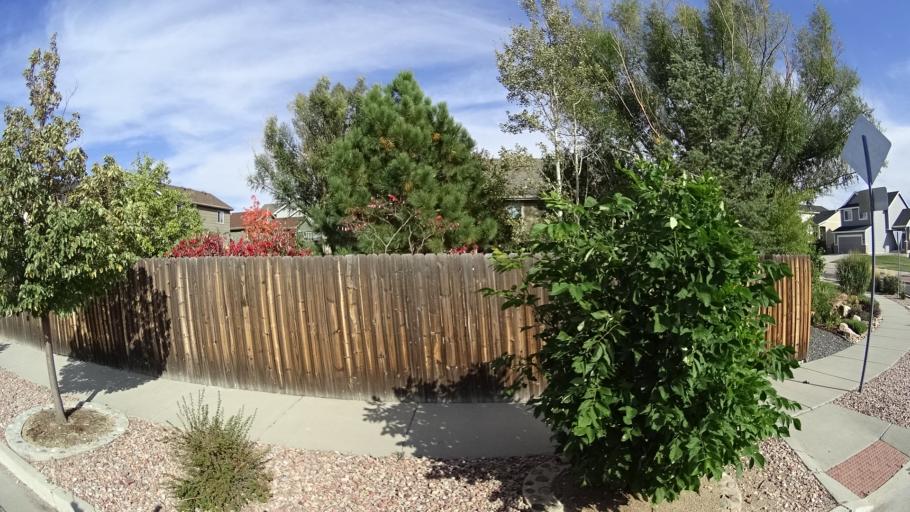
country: US
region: Colorado
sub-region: El Paso County
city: Cimarron Hills
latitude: 38.9085
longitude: -104.6861
